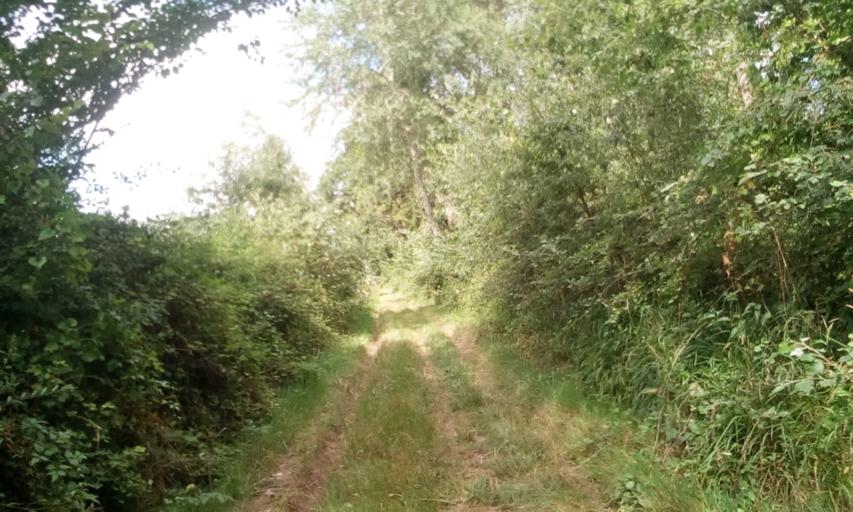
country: FR
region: Lower Normandy
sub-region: Departement du Calvados
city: Bellengreville
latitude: 49.1520
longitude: -0.2056
